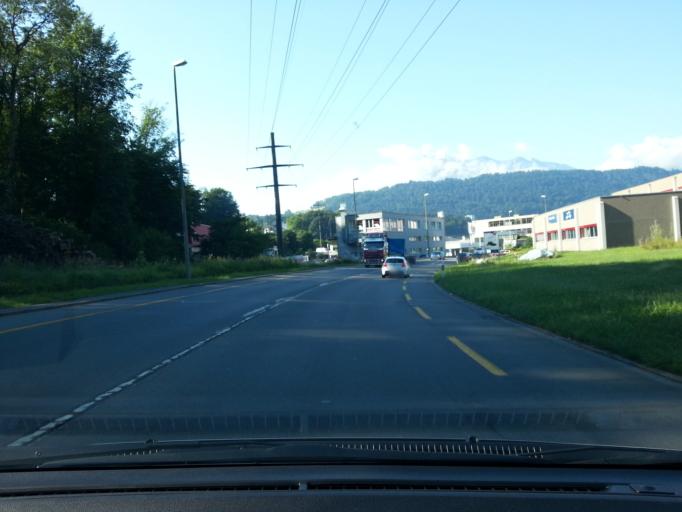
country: CH
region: Lucerne
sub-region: Hochdorf District
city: Emmen
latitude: 47.0683
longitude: 8.2700
